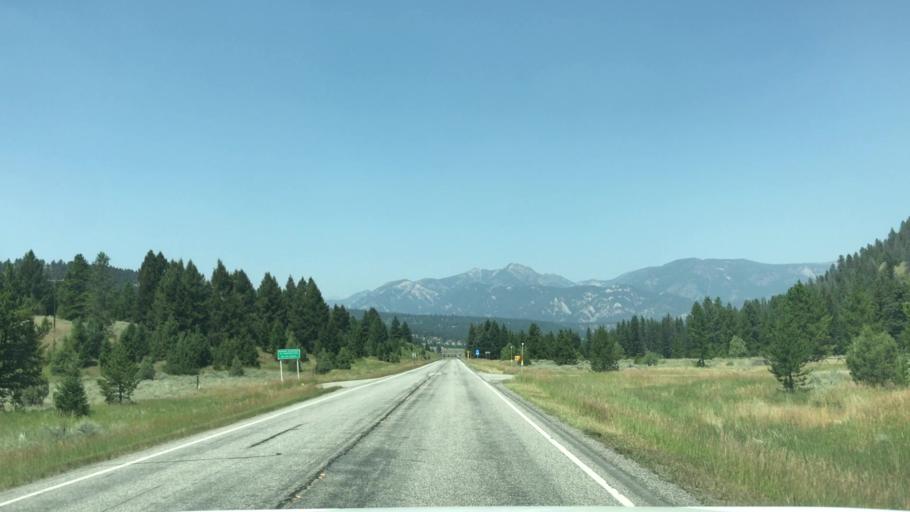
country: US
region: Montana
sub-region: Gallatin County
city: Big Sky
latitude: 45.2068
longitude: -111.2435
